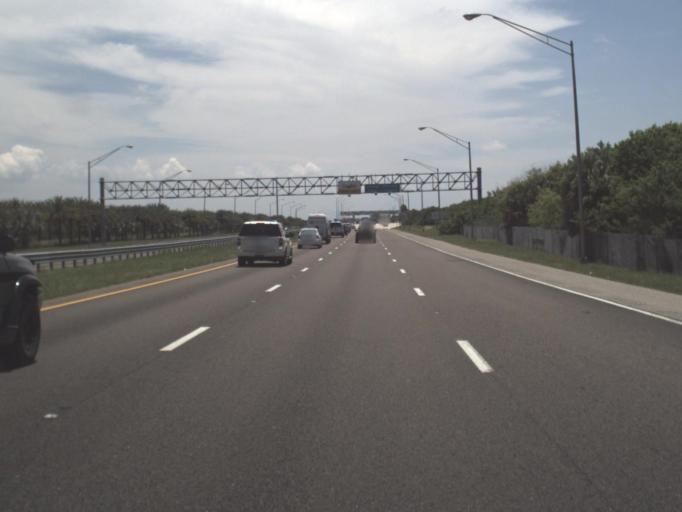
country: US
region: Florida
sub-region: Pinellas County
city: Tierra Verde
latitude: 27.6866
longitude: -82.6787
